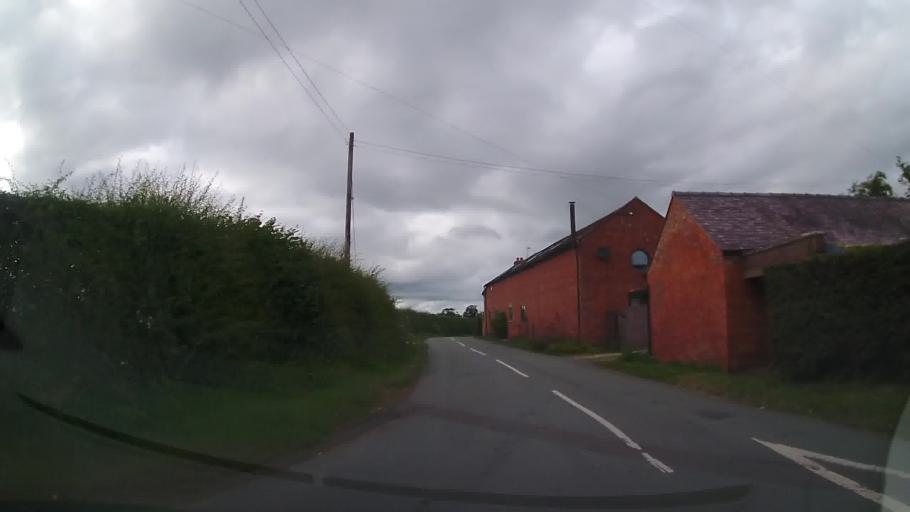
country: GB
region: England
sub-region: Shropshire
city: Wem
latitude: 52.9050
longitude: -2.7293
